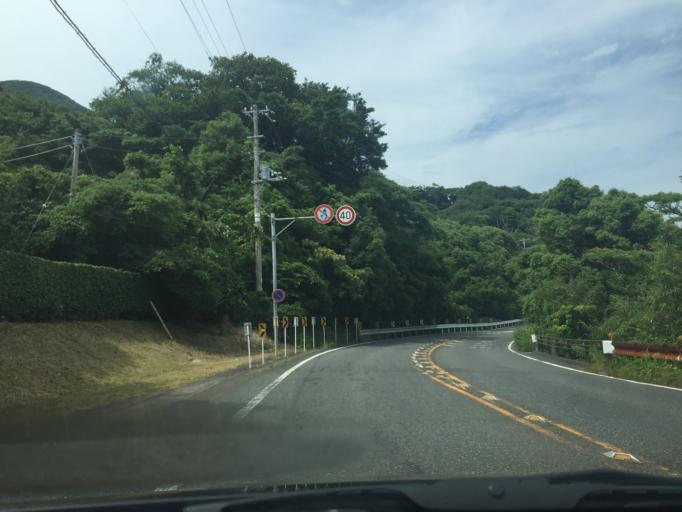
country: JP
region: Shizuoka
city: Shimoda
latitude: 34.7296
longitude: 138.9918
